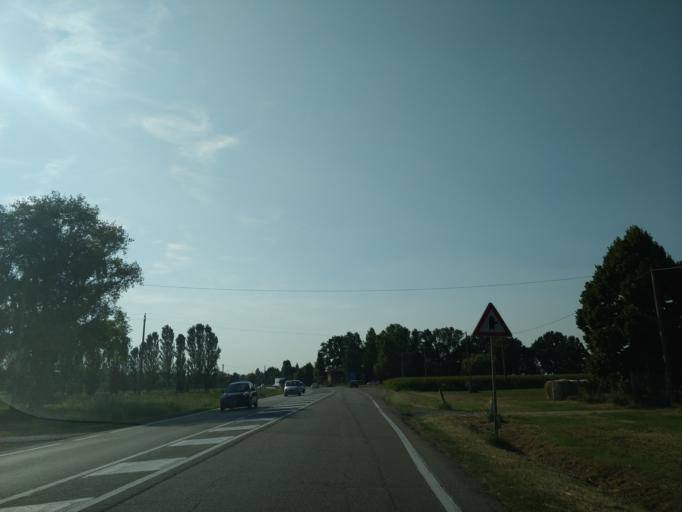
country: IT
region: Emilia-Romagna
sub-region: Provincia di Bologna
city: Argelato
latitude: 44.6051
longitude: 11.3351
